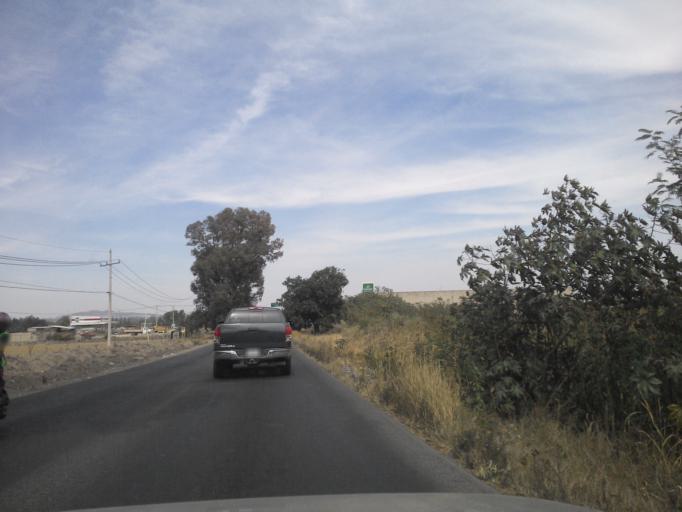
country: MX
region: Jalisco
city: San Sebastian el Grande
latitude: 20.5130
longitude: -103.4120
